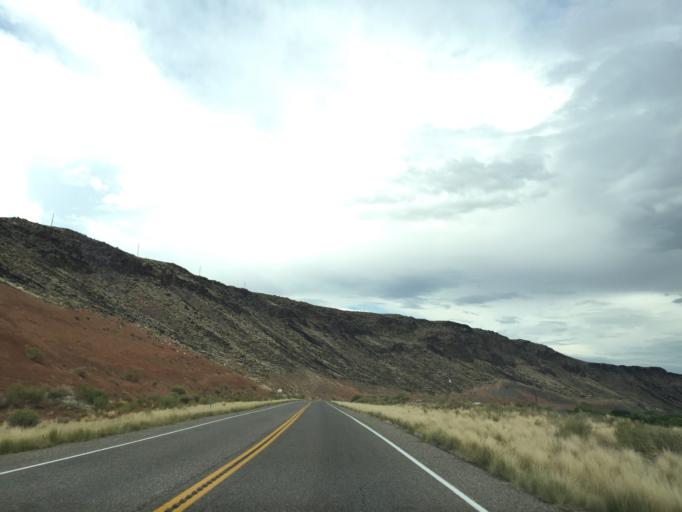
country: US
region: Utah
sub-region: Washington County
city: LaVerkin
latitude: 37.1951
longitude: -113.1526
